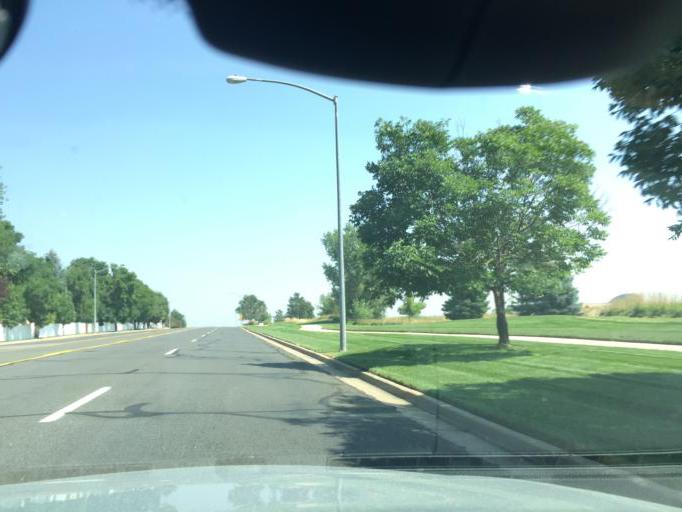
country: US
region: Colorado
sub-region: Adams County
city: Northglenn
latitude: 39.9082
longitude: -105.0061
